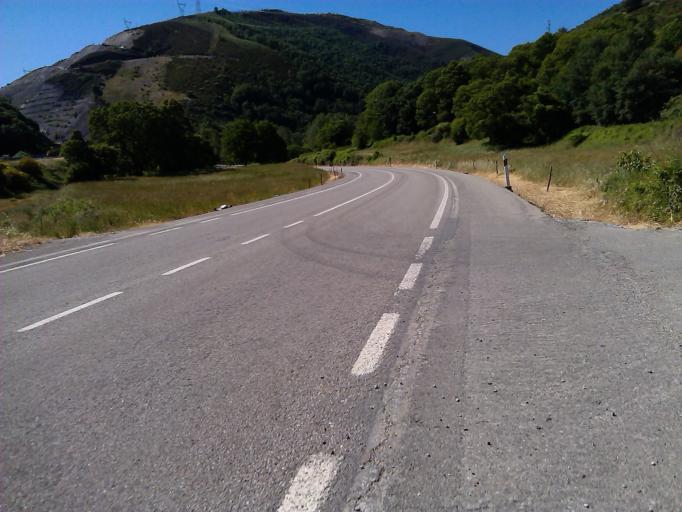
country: ES
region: Castille and Leon
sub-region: Provincia de Leon
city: Trabadelo
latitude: 42.6534
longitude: -6.8901
